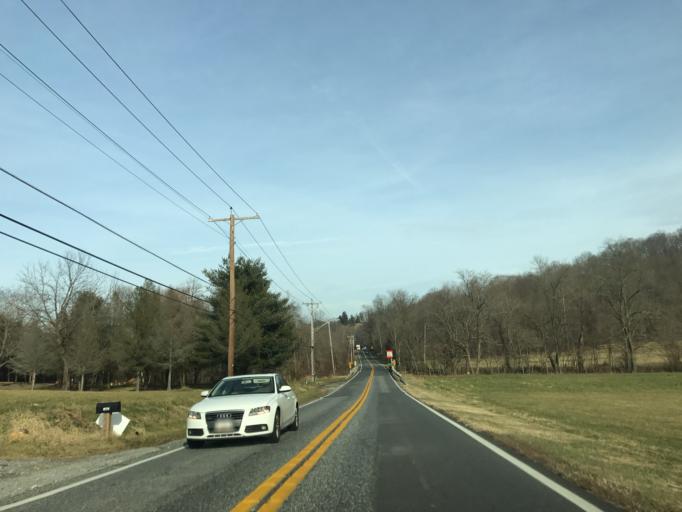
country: US
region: Maryland
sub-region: Baltimore County
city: Perry Hall
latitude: 39.4514
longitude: -76.4695
